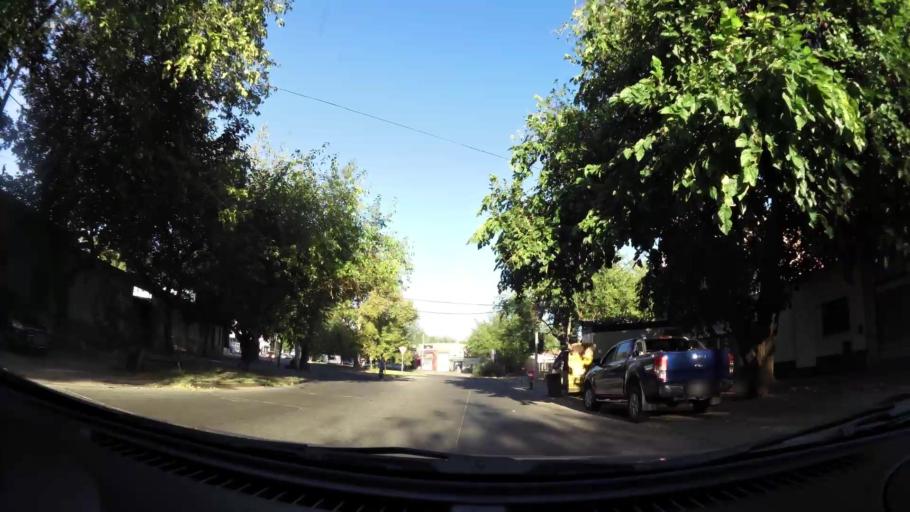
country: AR
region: Mendoza
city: Las Heras
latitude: -32.8664
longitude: -68.8284
